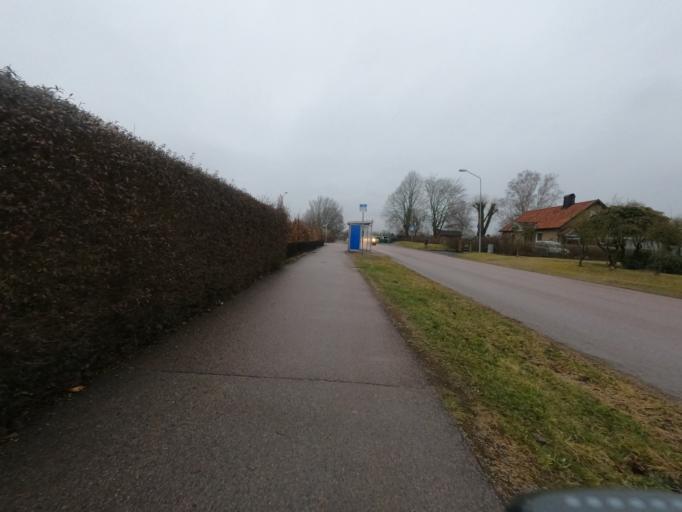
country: SE
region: Halland
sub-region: Halmstads Kommun
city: Fyllinge
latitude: 56.6763
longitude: 12.9250
